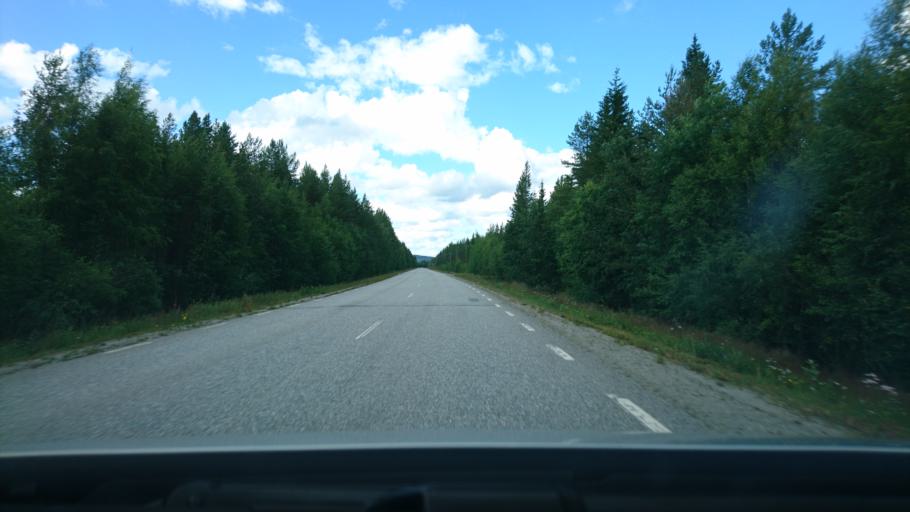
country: SE
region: Vaesterbotten
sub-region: Asele Kommun
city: Asele
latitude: 63.9837
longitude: 17.2653
